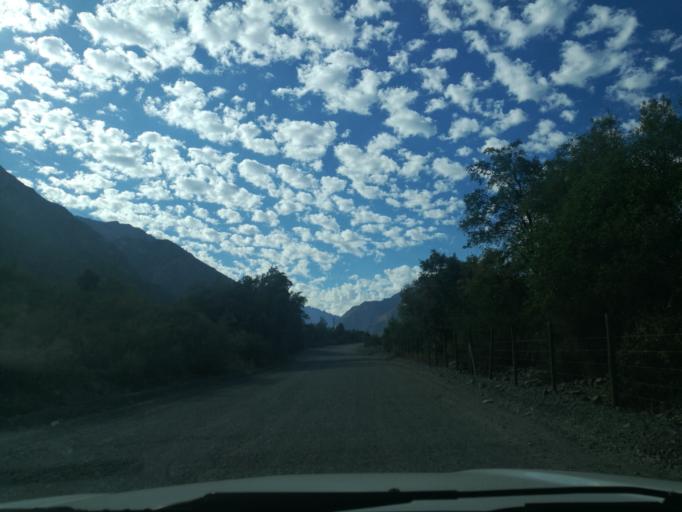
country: CL
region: O'Higgins
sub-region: Provincia de Cachapoal
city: Machali
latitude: -34.2956
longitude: -70.4308
